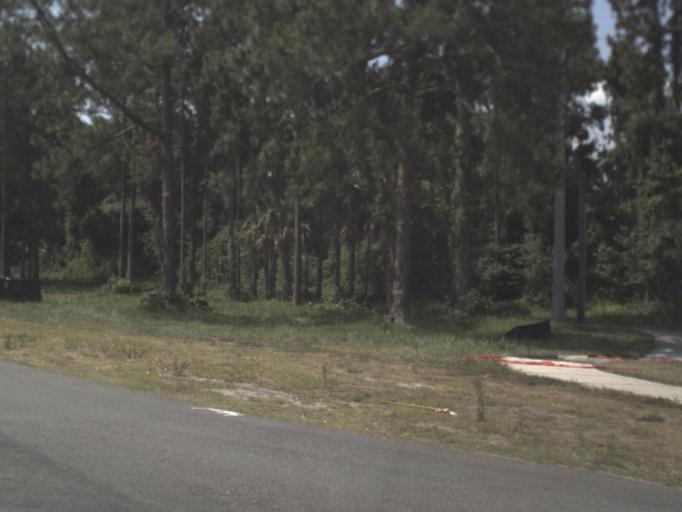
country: US
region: Florida
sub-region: Saint Johns County
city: Palm Valley
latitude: 30.1792
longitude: -81.3776
